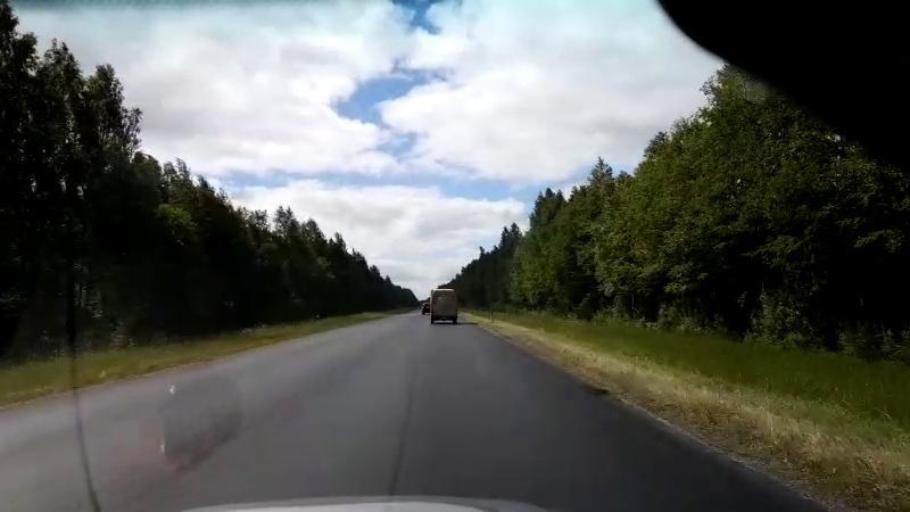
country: LV
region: Salacgrivas
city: Ainazi
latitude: 57.9605
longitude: 24.4434
